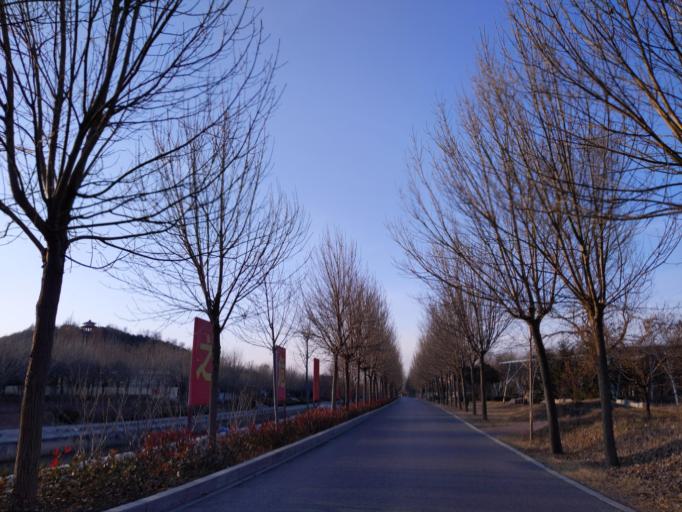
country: CN
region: Henan Sheng
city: Puyang
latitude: 35.7665
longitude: 115.0014
